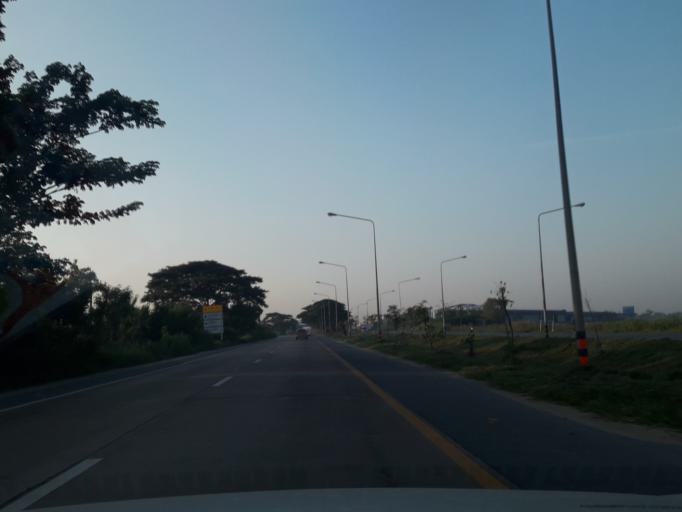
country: TH
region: Phra Nakhon Si Ayutthaya
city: Bang Ban
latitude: 14.3602
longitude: 100.5287
